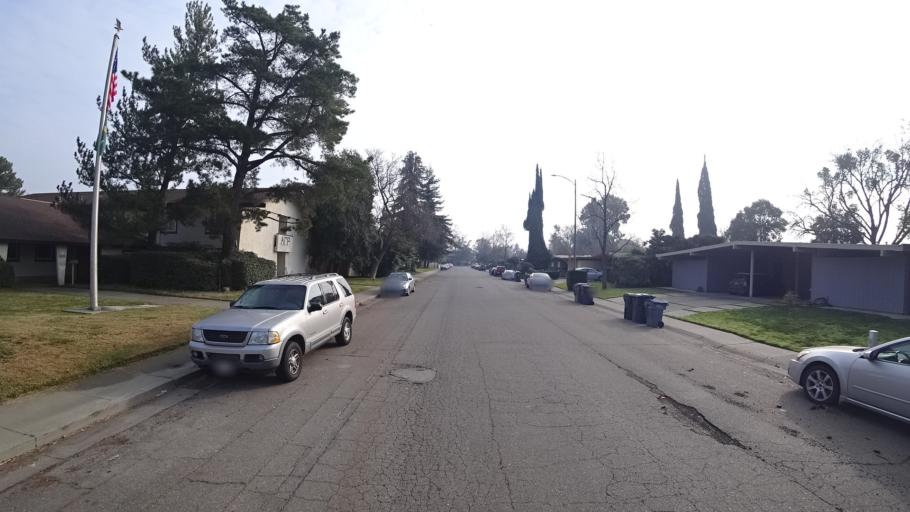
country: US
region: California
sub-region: Yolo County
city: Davis
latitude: 38.5601
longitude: -121.7628
